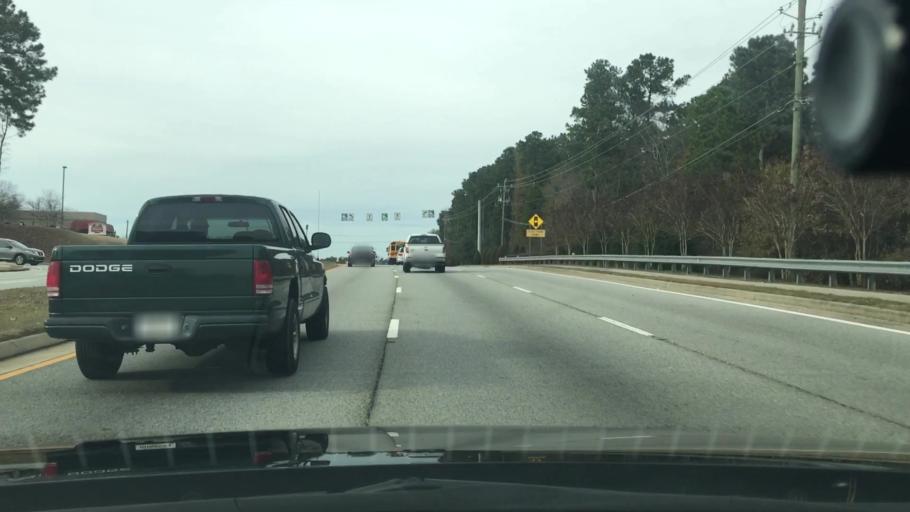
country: US
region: Georgia
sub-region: Fayette County
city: Peachtree City
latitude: 33.3947
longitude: -84.5872
